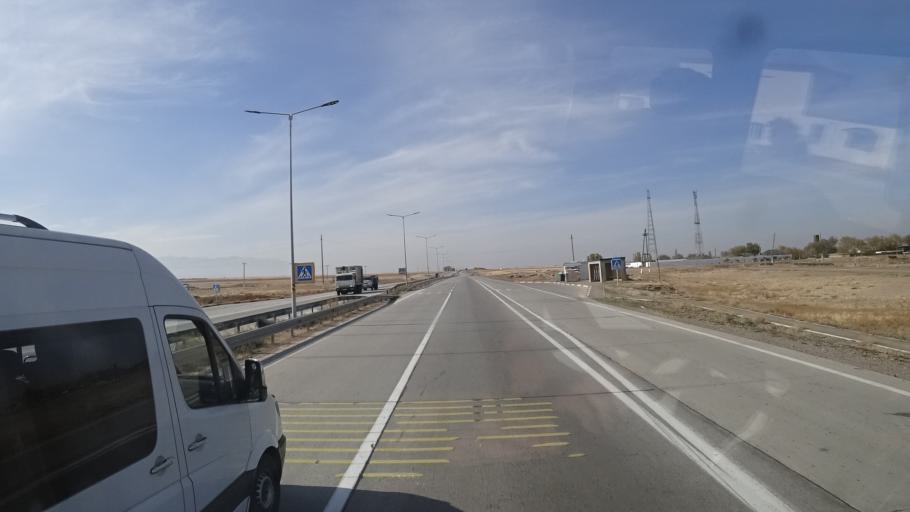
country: KZ
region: Zhambyl
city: Merke
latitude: 42.8893
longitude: 72.9860
